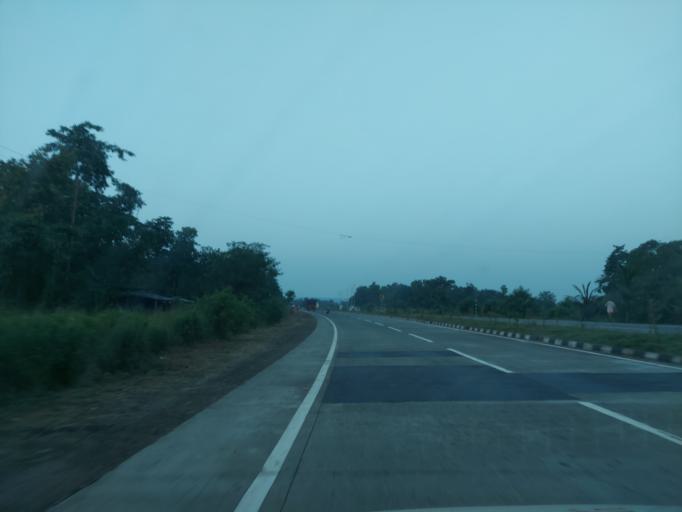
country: IN
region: Maharashtra
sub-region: Sindhudurg
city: Kudal
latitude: 16.1009
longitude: 73.7080
